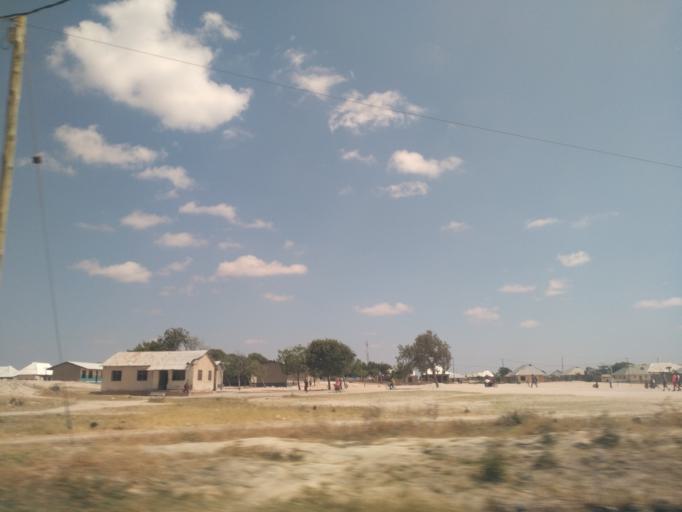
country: TZ
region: Dodoma
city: Dodoma
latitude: -6.1489
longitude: 35.7371
